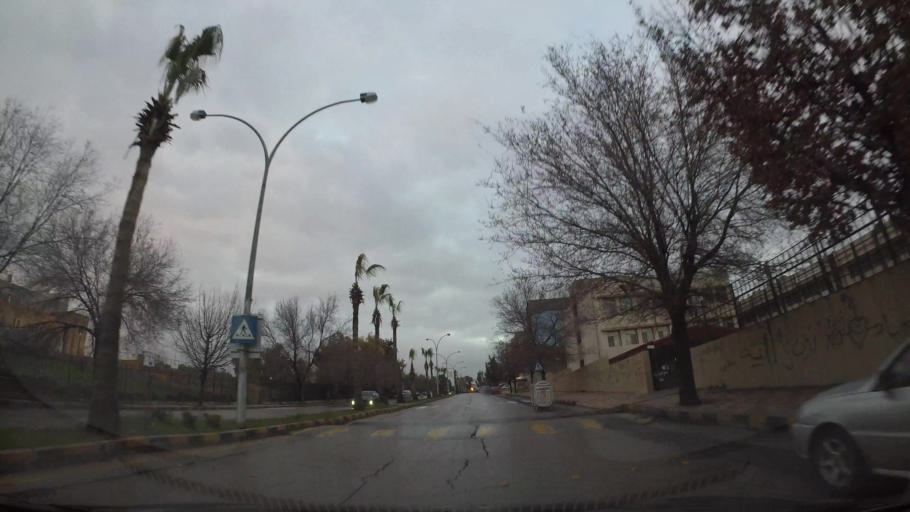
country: JO
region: Amman
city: Amman
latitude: 31.9823
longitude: 35.9107
